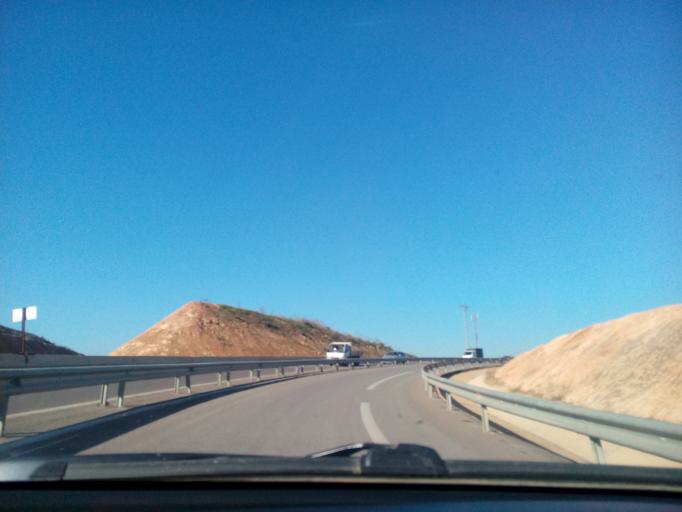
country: DZ
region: Chlef
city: Boukadir
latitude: 36.0532
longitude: 1.1377
